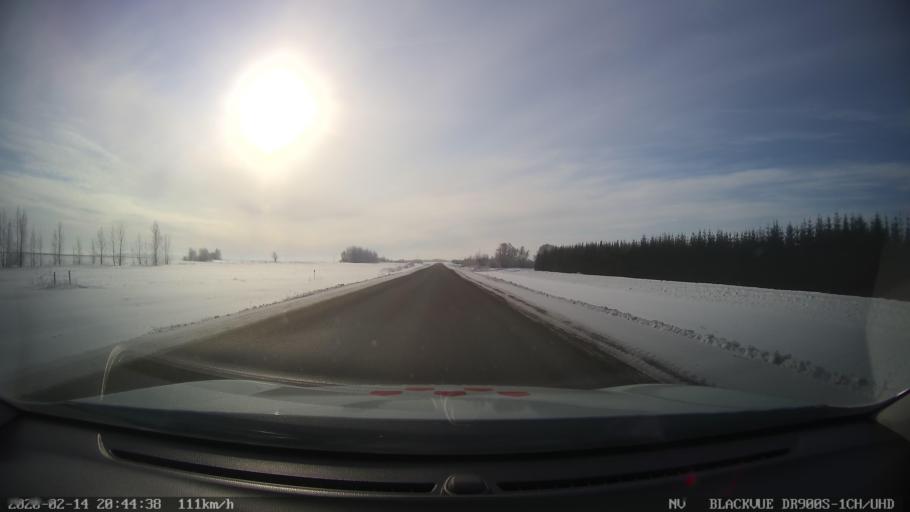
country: RU
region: Tatarstan
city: Kuybyshevskiy Zaton
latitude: 55.2904
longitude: 49.1454
